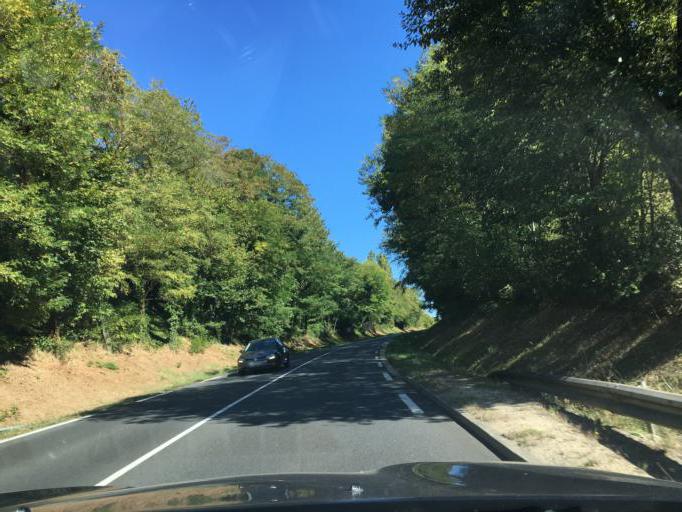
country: FR
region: Centre
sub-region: Departement d'Indre-et-Loire
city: Azay-le-Rideau
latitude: 47.2642
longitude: 0.4605
